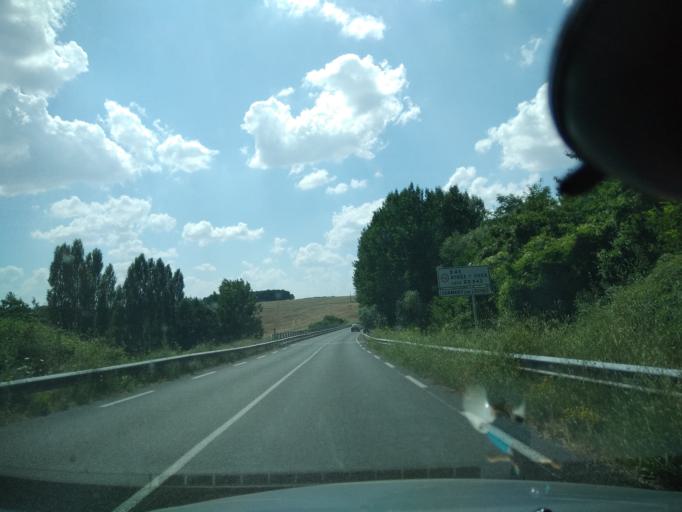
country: FR
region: Centre
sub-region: Departement d'Indre-et-Loire
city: Blere
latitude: 47.3157
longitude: 1.0003
